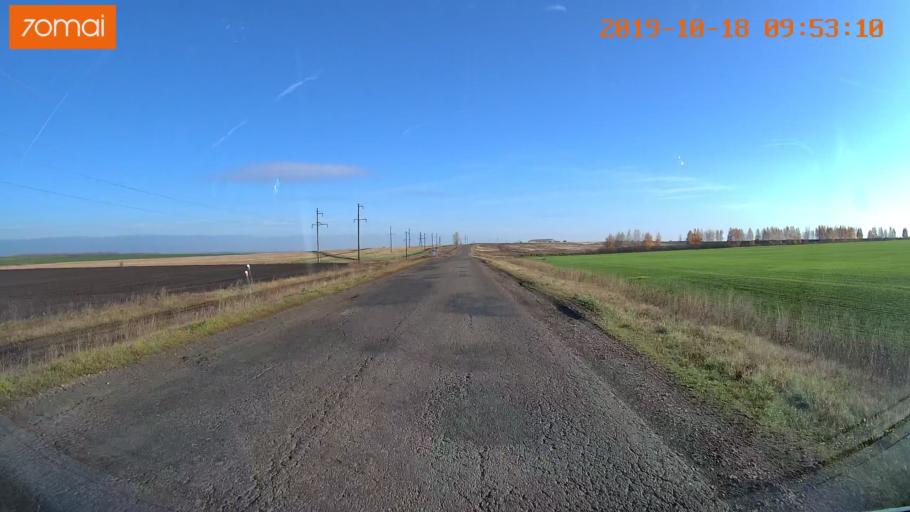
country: RU
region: Tula
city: Kazachka
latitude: 53.3584
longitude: 38.3235
